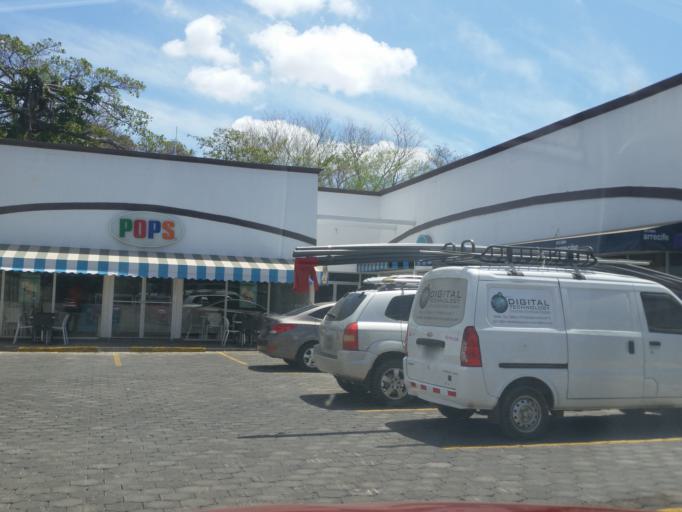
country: NI
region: Managua
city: Managua
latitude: 12.0987
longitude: -86.2481
